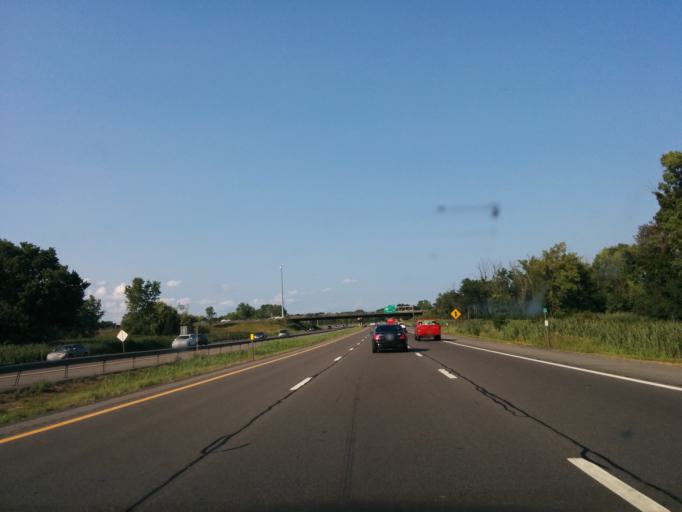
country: US
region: New York
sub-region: Onondaga County
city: North Syracuse
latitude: 43.1389
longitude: -76.1153
